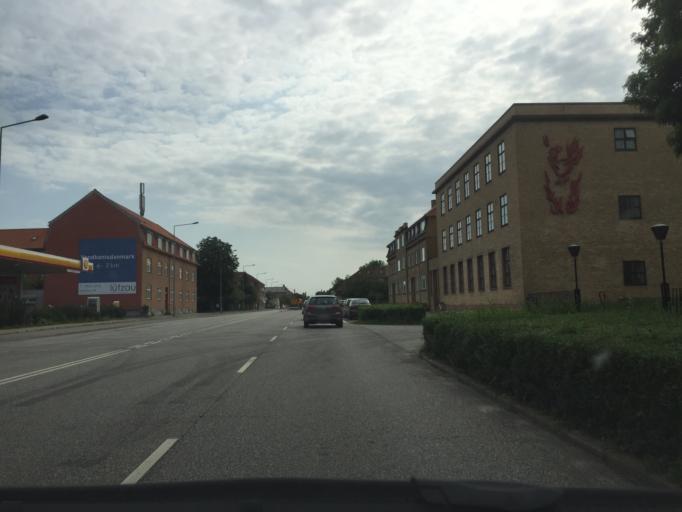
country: DK
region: Capital Region
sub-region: Gentofte Kommune
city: Charlottenlund
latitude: 55.7489
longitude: 12.5573
